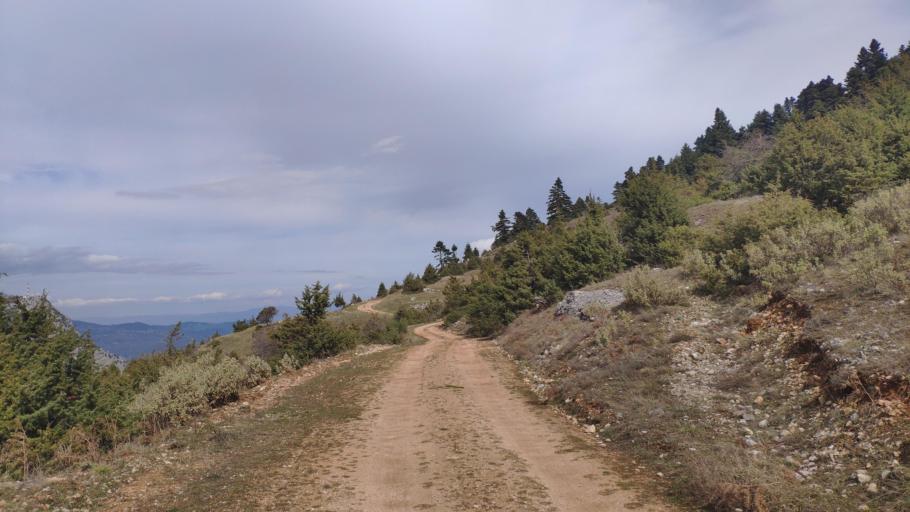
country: GR
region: Central Greece
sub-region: Nomos Fokidos
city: Amfissa
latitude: 38.6464
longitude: 22.4266
